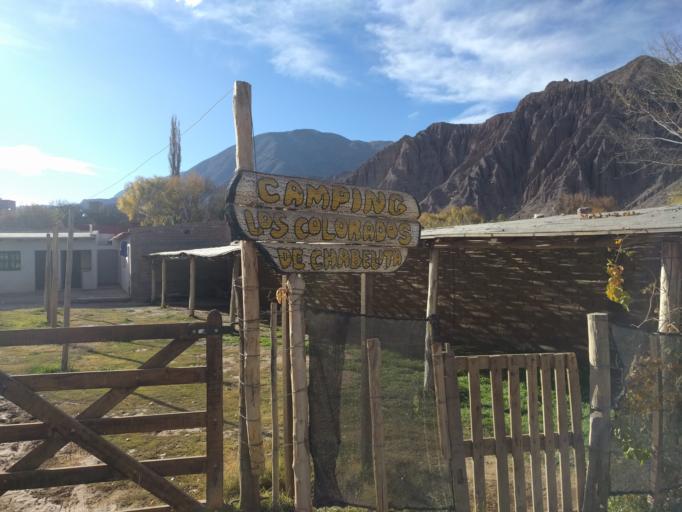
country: AR
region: Jujuy
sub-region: Departamento de Tumbaya
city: Tumbaya
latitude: -23.7423
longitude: -65.5051
